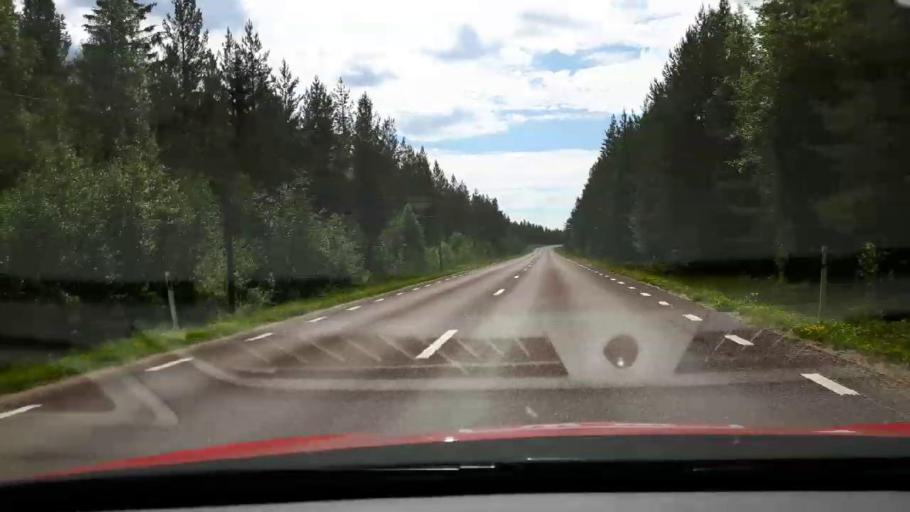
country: SE
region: Jaemtland
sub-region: Harjedalens Kommun
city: Sveg
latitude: 62.1100
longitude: 14.9707
